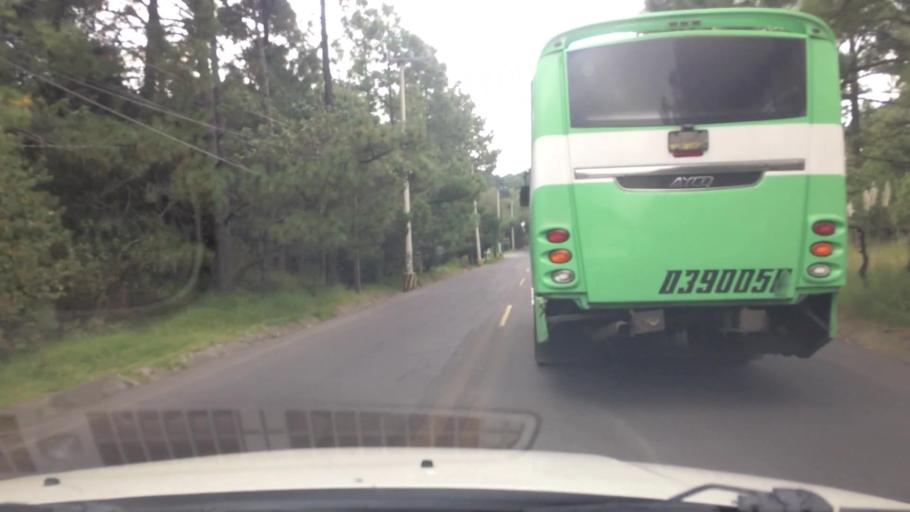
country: MX
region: Mexico City
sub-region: Tlalpan
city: Lomas de Tepemecatl
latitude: 19.2516
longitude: -99.2440
